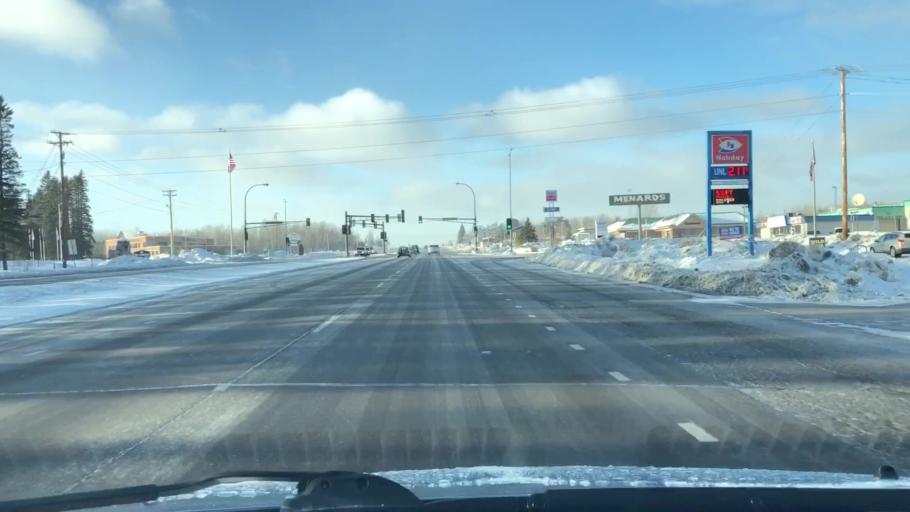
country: US
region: Minnesota
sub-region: Saint Louis County
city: Hermantown
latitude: 46.8214
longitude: -92.1853
